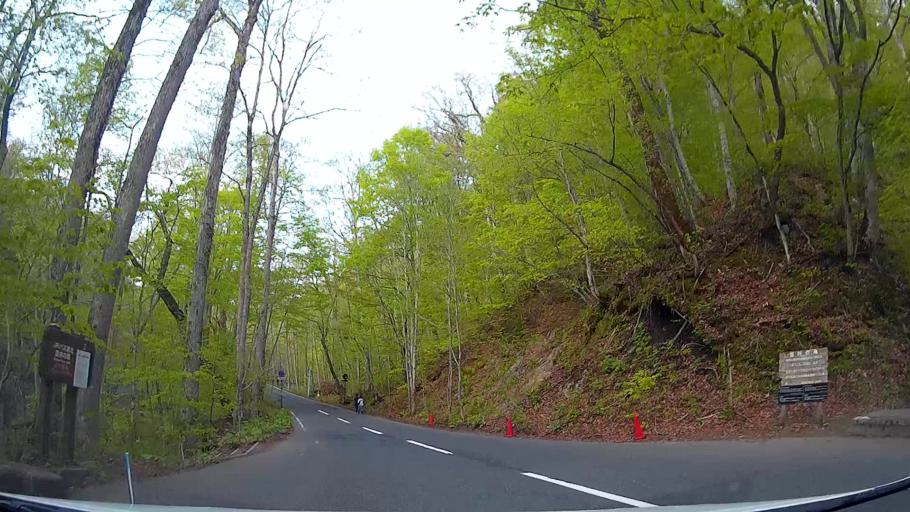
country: JP
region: Aomori
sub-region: Aomori Shi
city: Furudate
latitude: 40.5211
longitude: 140.9722
